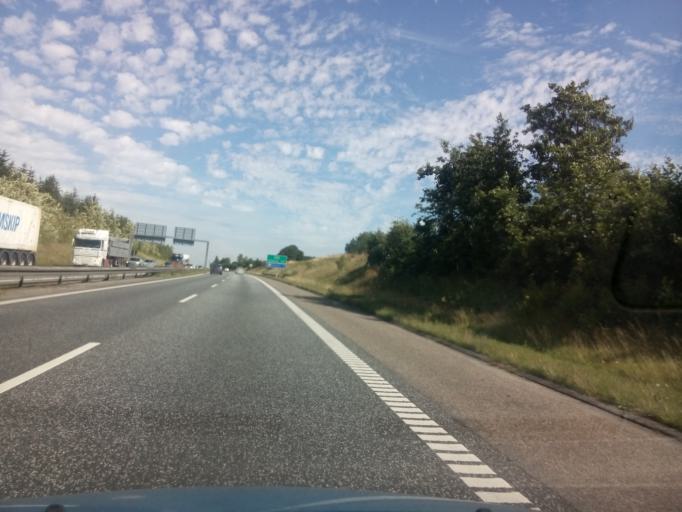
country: DK
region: Central Jutland
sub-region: Arhus Kommune
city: Trige
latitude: 56.2336
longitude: 10.1250
